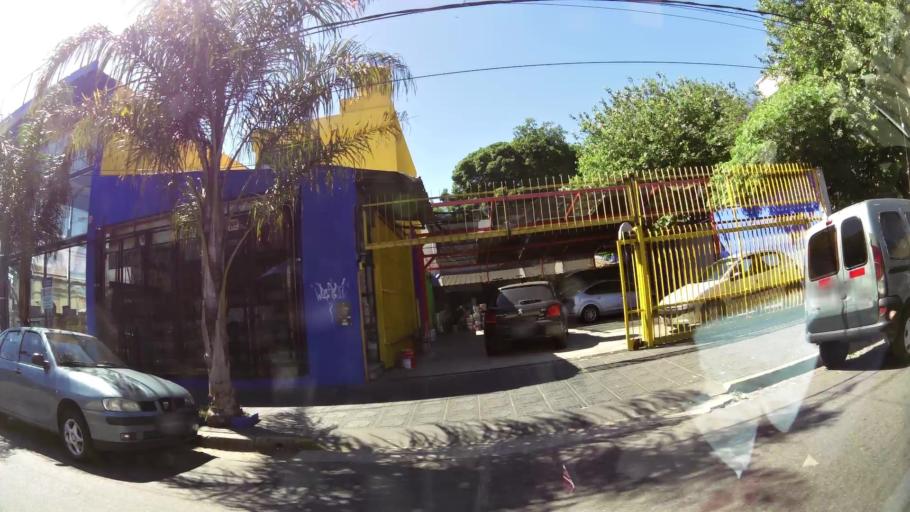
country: AR
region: Buenos Aires
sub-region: Partido de General San Martin
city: General San Martin
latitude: -34.5806
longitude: -58.5428
